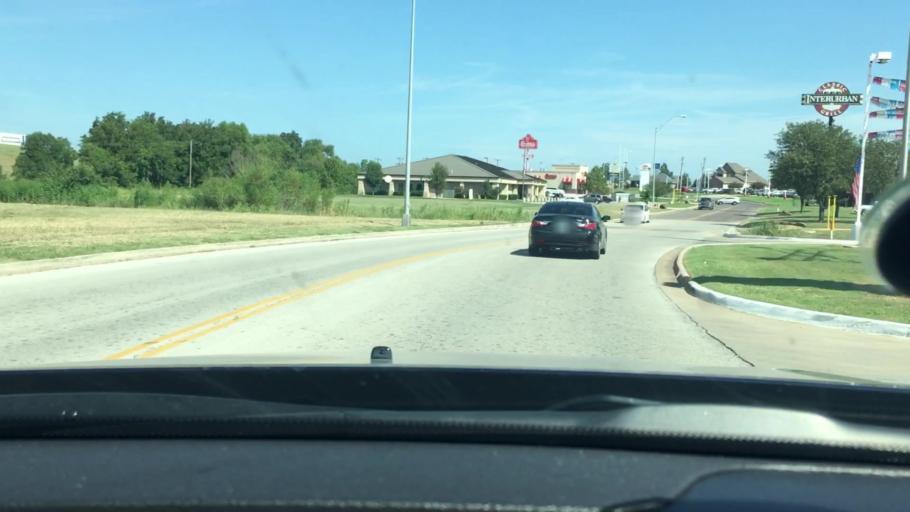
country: US
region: Oklahoma
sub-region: Carter County
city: Ardmore
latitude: 34.1783
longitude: -97.1662
